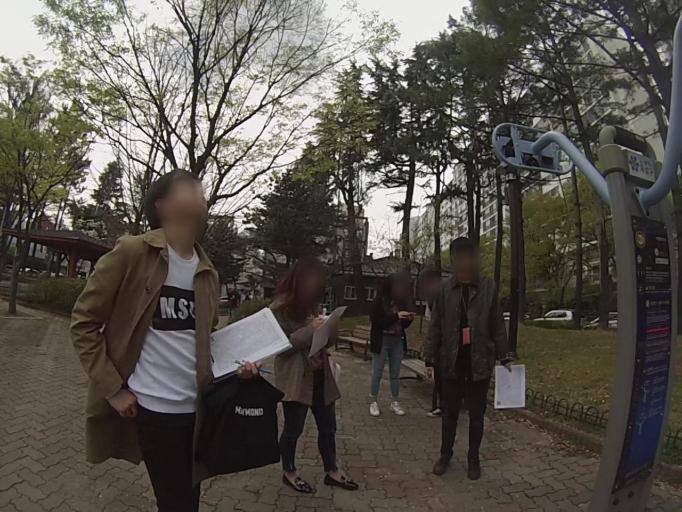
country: KR
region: Daejeon
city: Songgang-dong
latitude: 36.3619
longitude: 127.3551
